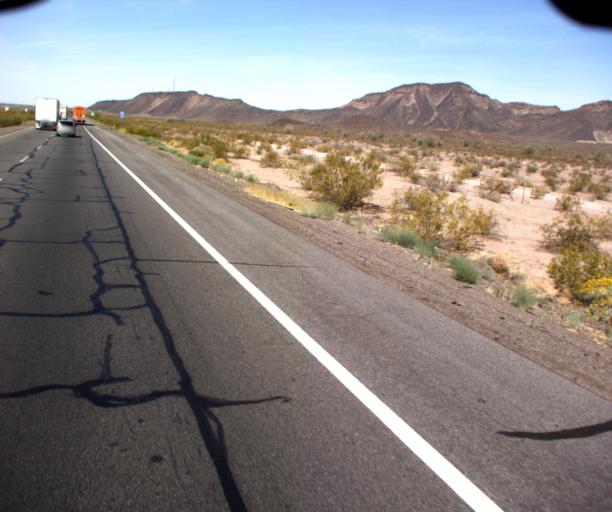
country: US
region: Arizona
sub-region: Maricopa County
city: Buckeye
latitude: 33.5219
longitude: -113.0757
